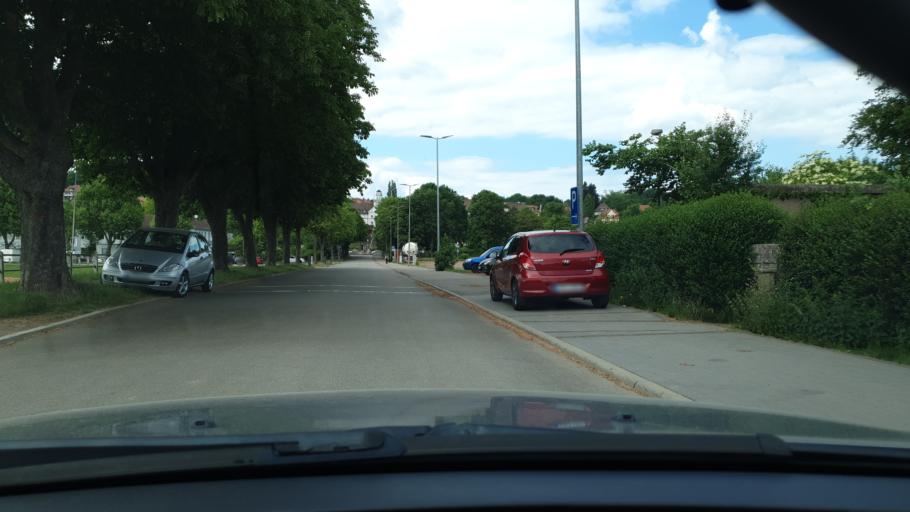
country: DE
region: Rheinland-Pfalz
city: Zweibrucken
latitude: 49.2540
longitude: 7.3758
